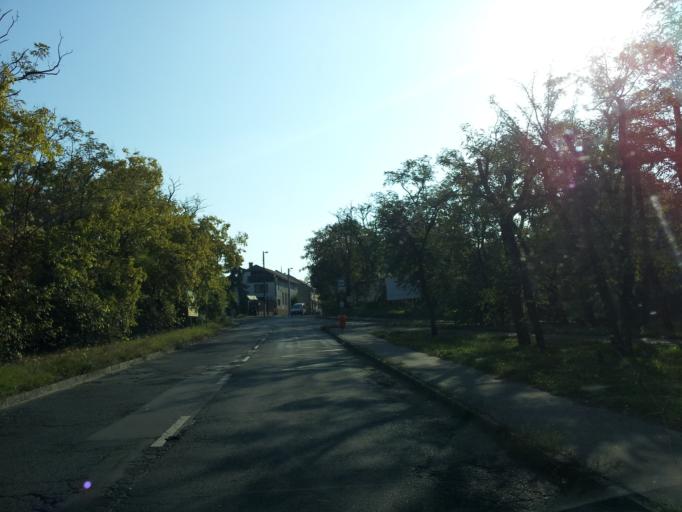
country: HU
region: Budapest
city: Budapest X. keruelet
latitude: 47.4679
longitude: 19.1787
